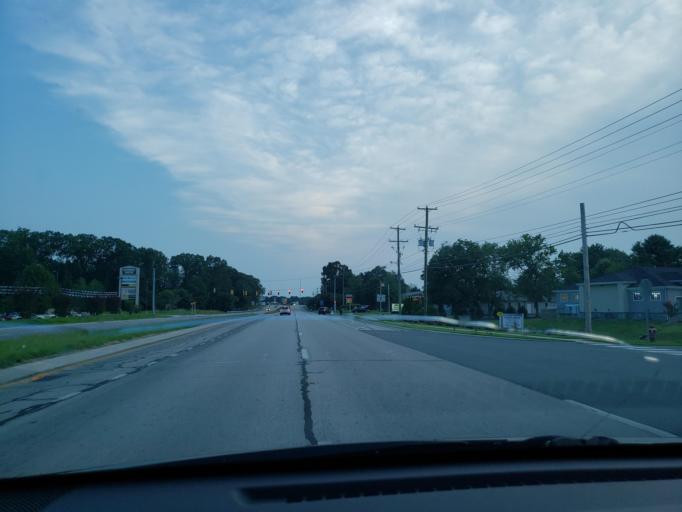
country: US
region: Delaware
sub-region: Kent County
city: Dover Base Housing
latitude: 39.1243
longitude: -75.4993
